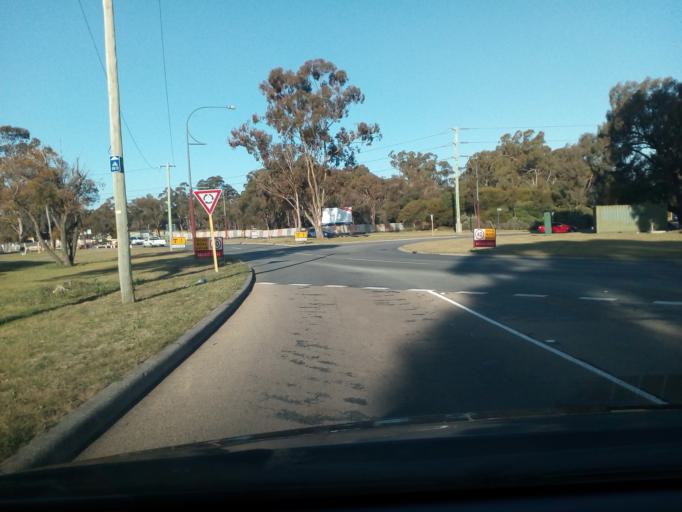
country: AU
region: Western Australia
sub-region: Kwinana
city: Parmelia
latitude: -32.2541
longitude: 115.8106
